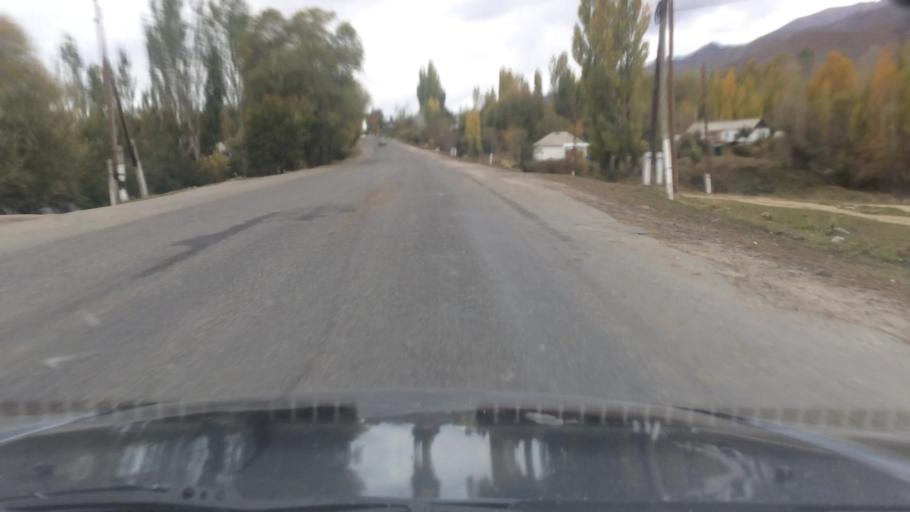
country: KG
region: Ysyk-Koel
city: Tyup
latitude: 42.7485
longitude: 78.1179
